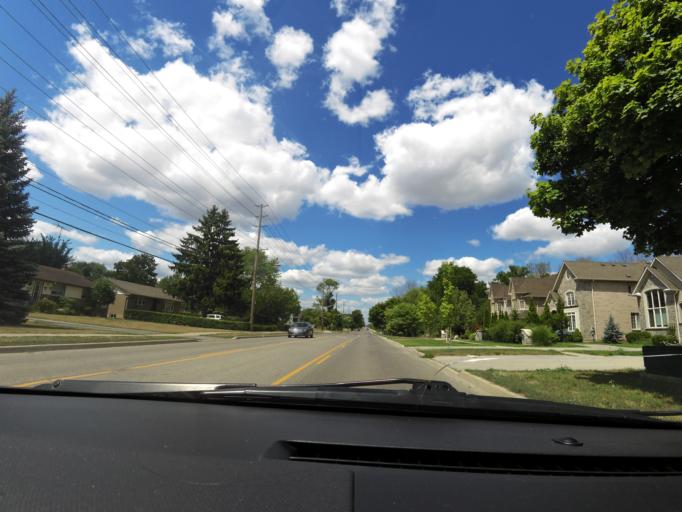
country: CA
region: Ontario
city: Oakville
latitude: 43.3755
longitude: -79.7294
